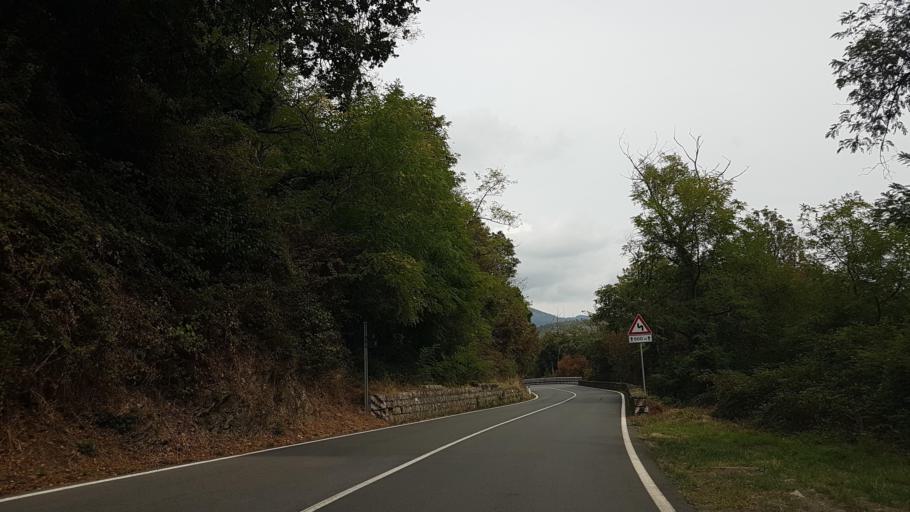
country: IT
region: Liguria
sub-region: Provincia di Genova
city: Casarza Ligure
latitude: 44.2574
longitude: 9.4622
